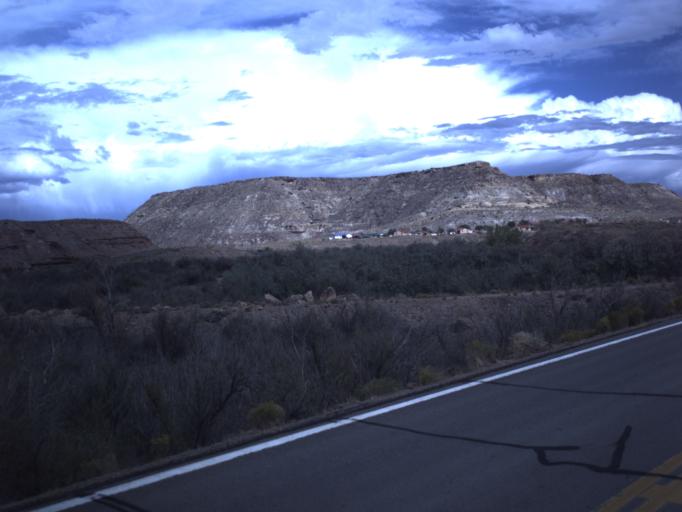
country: US
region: Colorado
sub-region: Montezuma County
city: Towaoc
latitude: 37.2188
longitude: -109.1916
